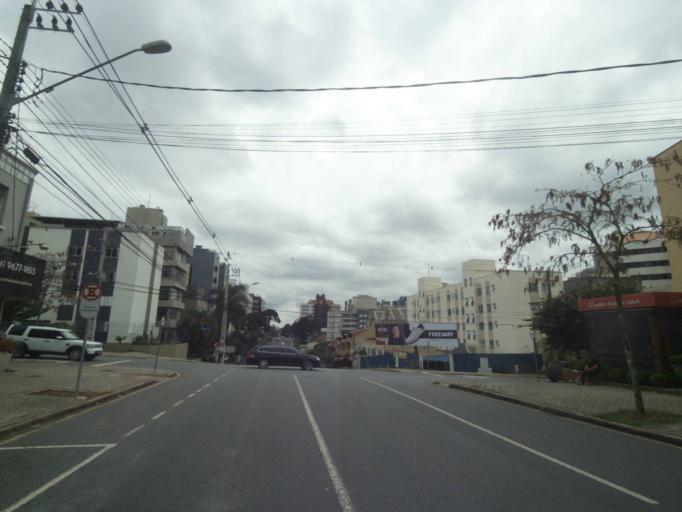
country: BR
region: Parana
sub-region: Curitiba
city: Curitiba
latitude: -25.4339
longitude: -49.2952
